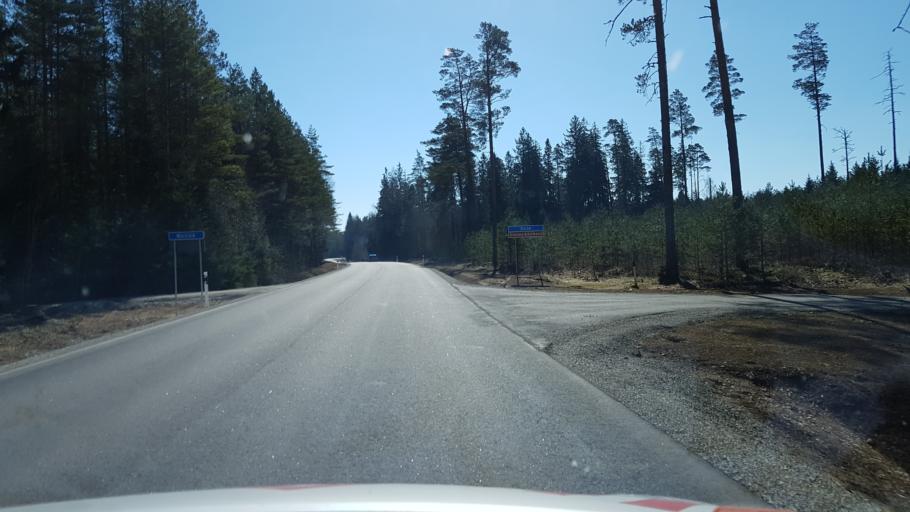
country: EE
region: Laeaene-Virumaa
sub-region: Vinni vald
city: Vinni
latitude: 59.1300
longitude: 26.6081
